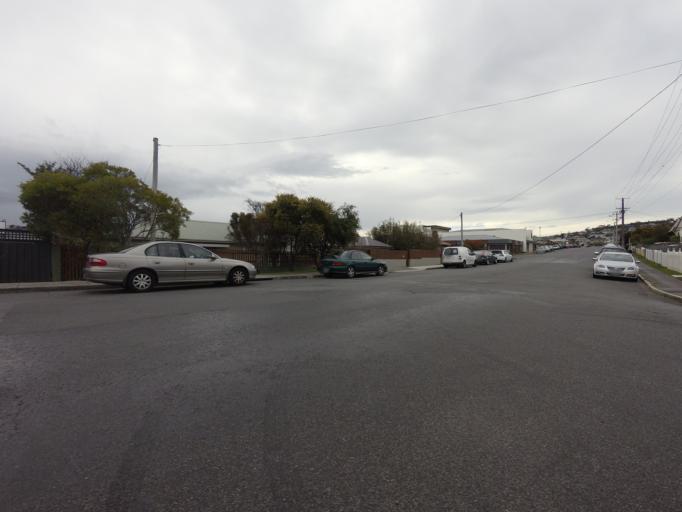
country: AU
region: Tasmania
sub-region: Clarence
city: Bellerive
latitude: -42.8766
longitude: 147.3697
